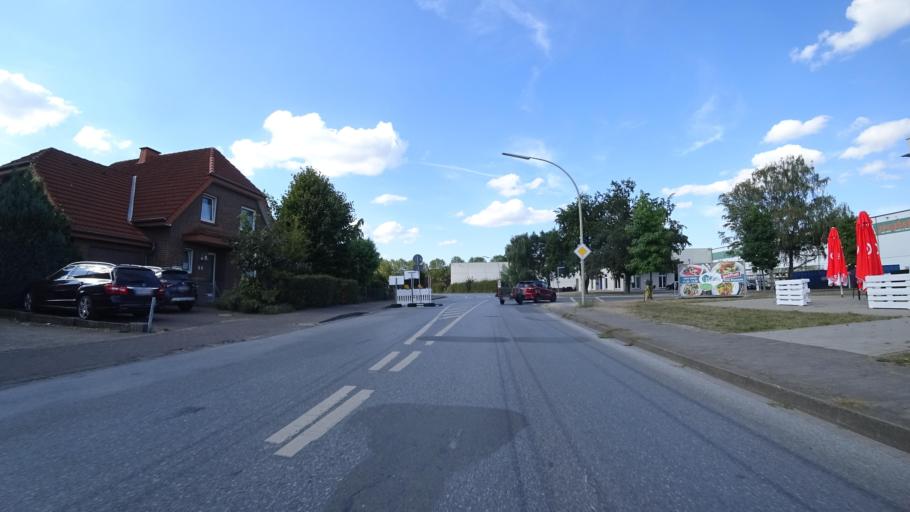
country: DE
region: North Rhine-Westphalia
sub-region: Regierungsbezirk Detmold
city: Rheda-Wiedenbruck
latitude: 51.8506
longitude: 8.3095
